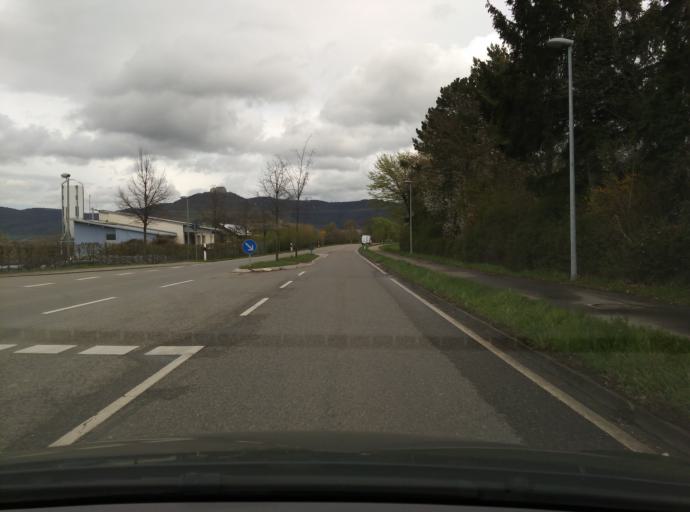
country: DE
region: Baden-Wuerttemberg
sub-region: Regierungsbezirk Stuttgart
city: Kohlberg
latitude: 48.5594
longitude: 9.3454
